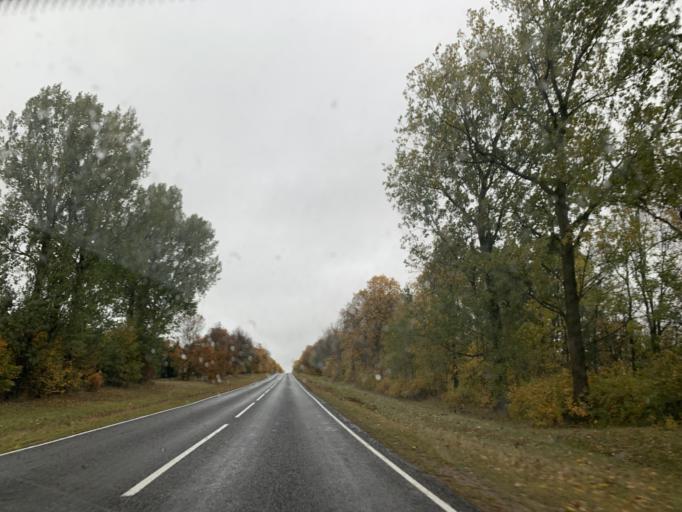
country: BY
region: Minsk
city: Novy Svyerzhan'
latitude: 53.4323
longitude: 26.6449
